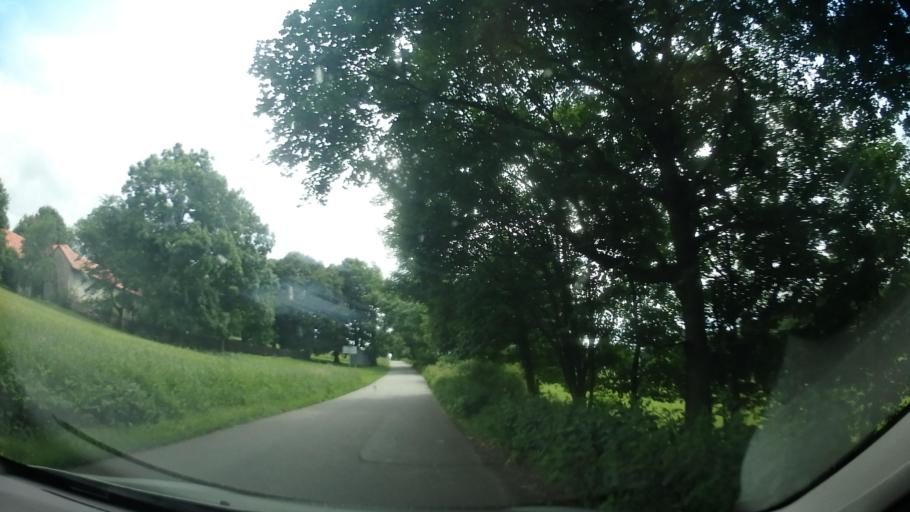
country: CZ
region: Vysocina
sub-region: Okres Zd'ar nad Sazavou
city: Nove Mesto na Morave
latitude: 49.5996
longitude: 16.0618
